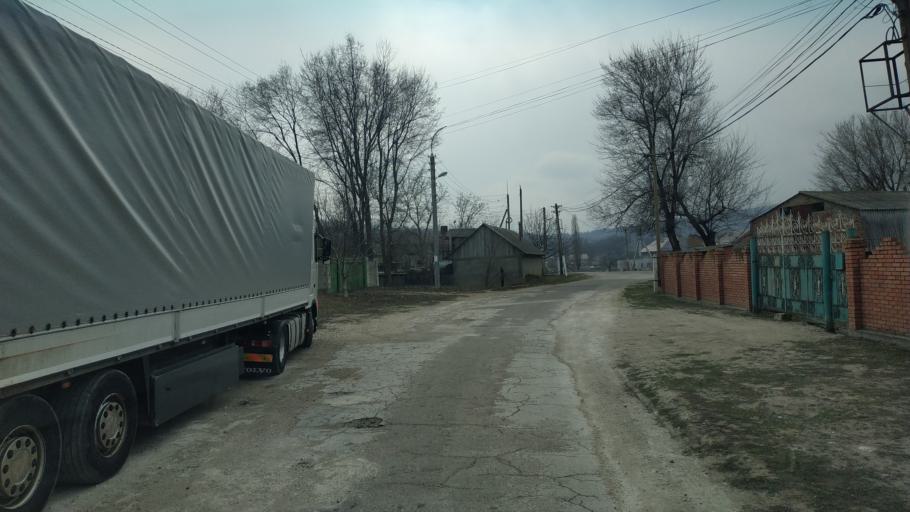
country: MD
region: Chisinau
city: Singera
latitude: 46.9183
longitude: 28.9826
